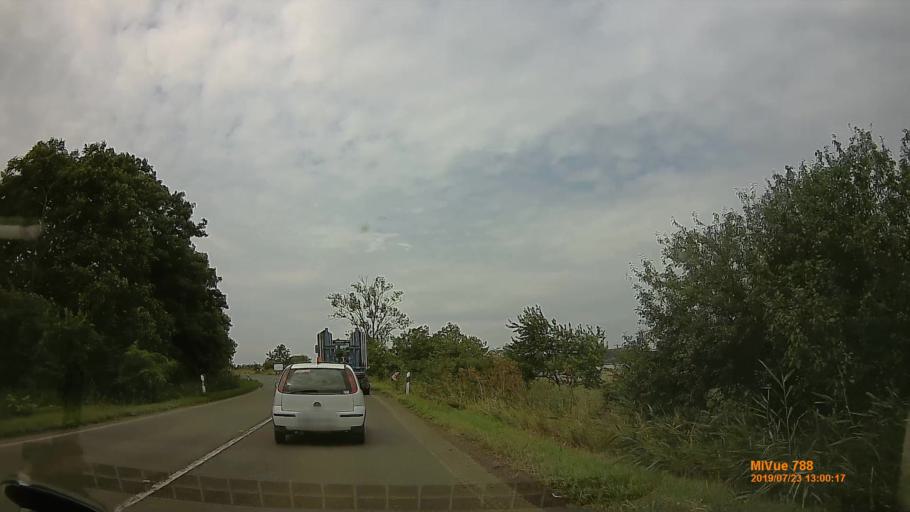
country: HU
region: Szabolcs-Szatmar-Bereg
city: Tiszalok
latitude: 47.9583
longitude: 21.4236
